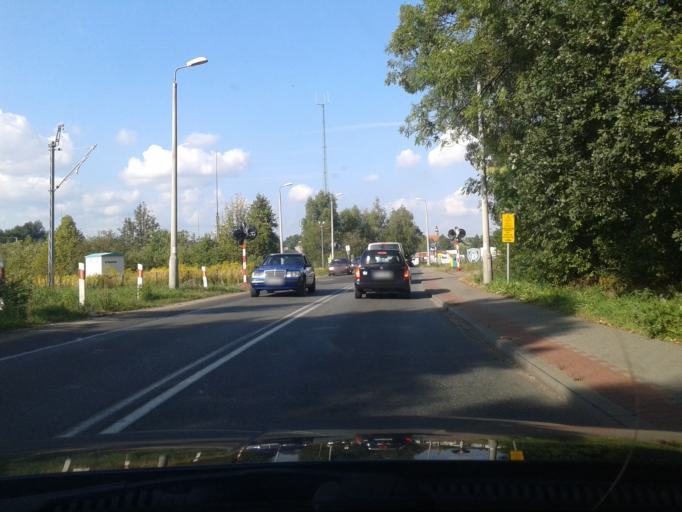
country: PL
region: Silesian Voivodeship
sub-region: Powiat wodzislawski
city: Wodzislaw Slaski
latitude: 49.9916
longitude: 18.4553
